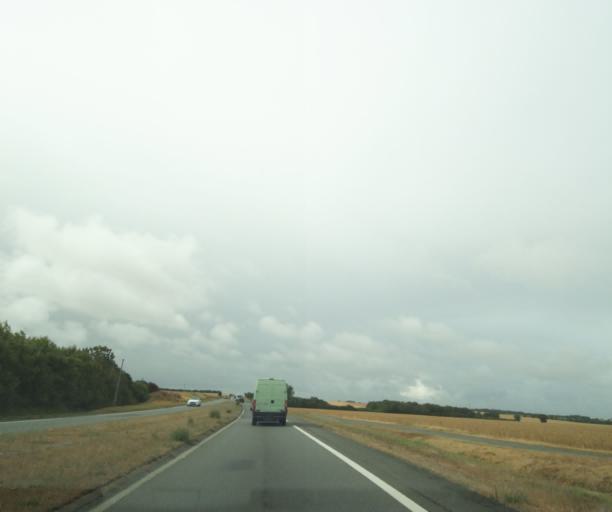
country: FR
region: Poitou-Charentes
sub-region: Departement de la Charente-Maritime
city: Marsilly
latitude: 46.2089
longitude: -1.1366
